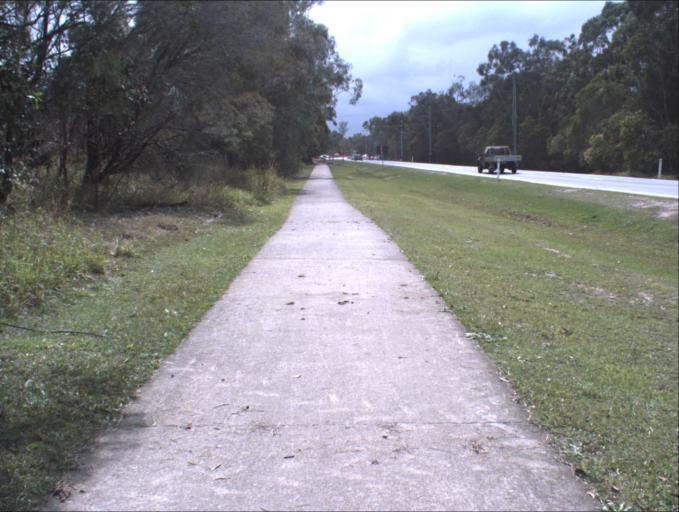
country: AU
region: Queensland
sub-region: Logan
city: Woodridge
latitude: -27.6760
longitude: 153.0704
